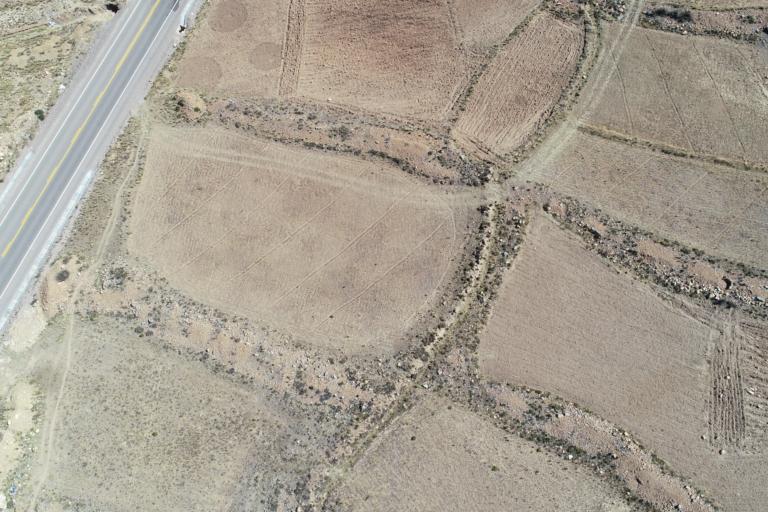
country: BO
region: La Paz
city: Achacachi
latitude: -15.8853
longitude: -68.8107
